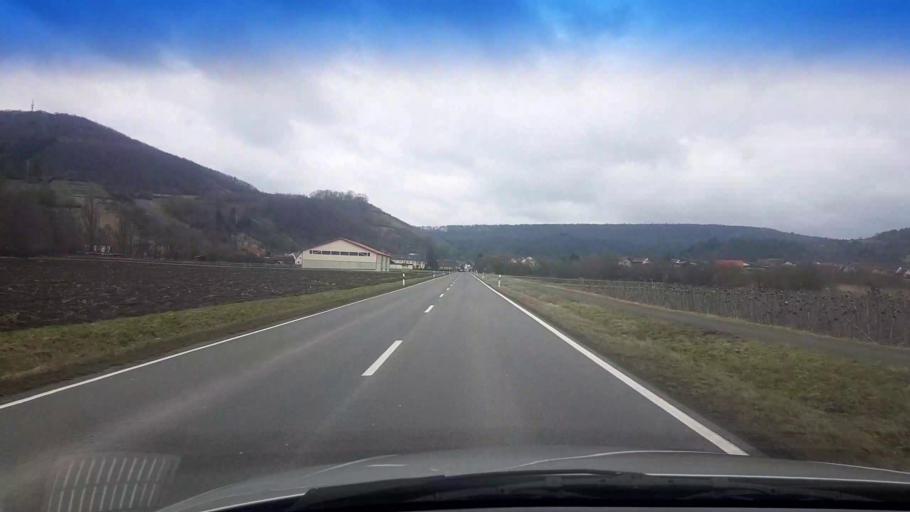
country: DE
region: Bavaria
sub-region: Regierungsbezirk Unterfranken
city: Knetzgau
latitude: 49.9734
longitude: 10.5610
